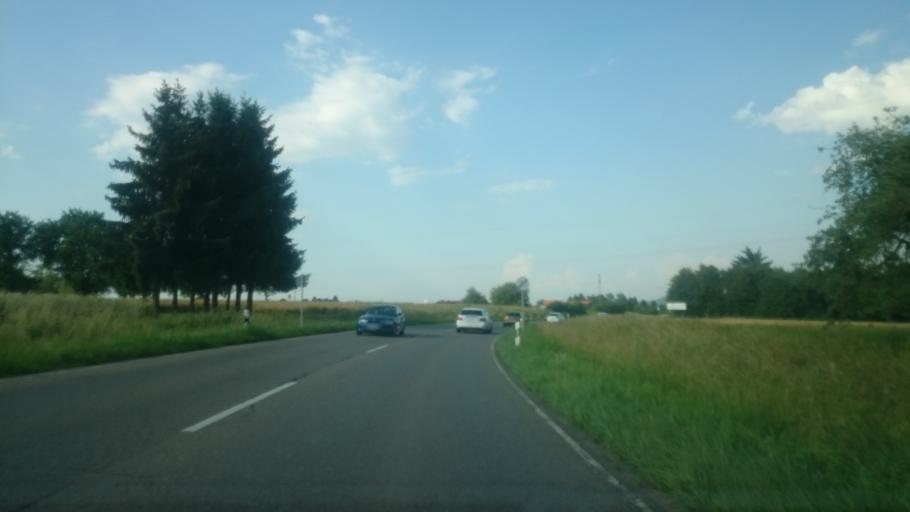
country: DE
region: Baden-Wuerttemberg
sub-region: Tuebingen Region
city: Mossingen
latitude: 48.4209
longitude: 9.0570
